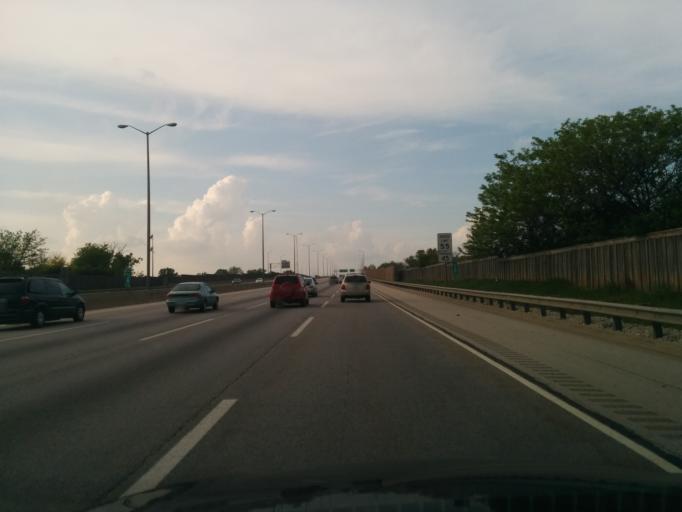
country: US
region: Illinois
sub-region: DuPage County
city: Glendale Heights
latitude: 41.9117
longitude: -88.0378
